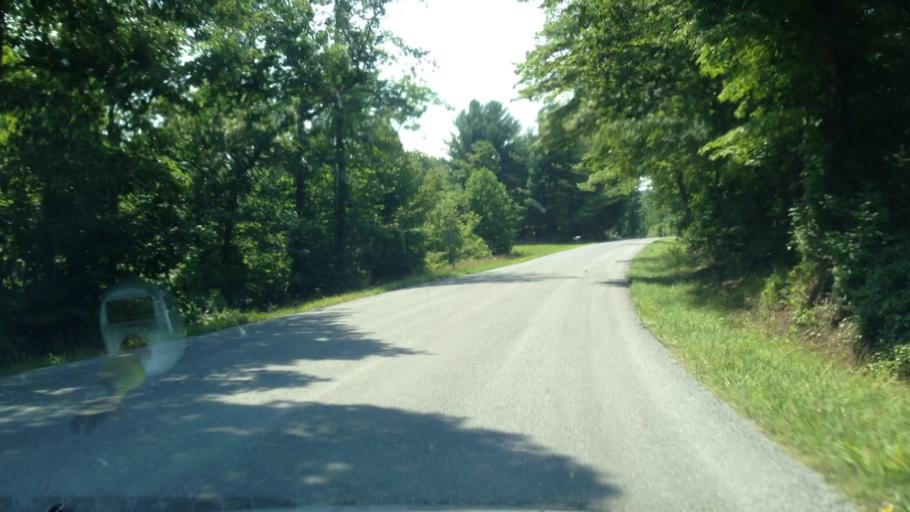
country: US
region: Virginia
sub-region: Patrick County
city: Stuart
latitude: 36.5933
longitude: -80.2899
